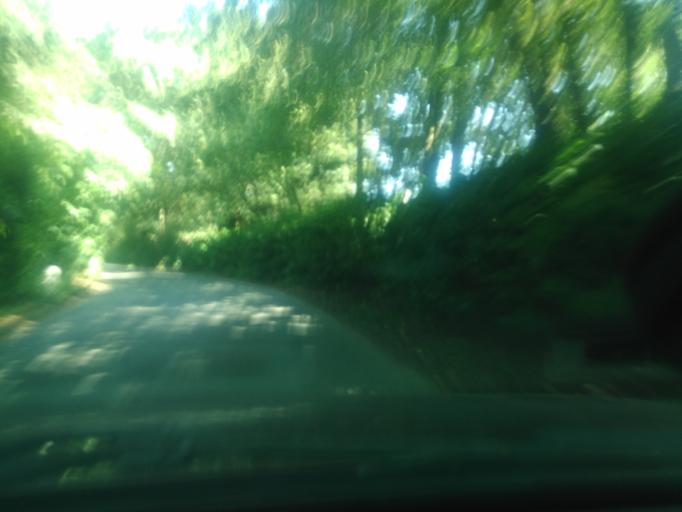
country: FR
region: Pays de la Loire
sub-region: Departement de la Vendee
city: Dompierre-sur-Yon
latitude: 46.7221
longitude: -1.3800
